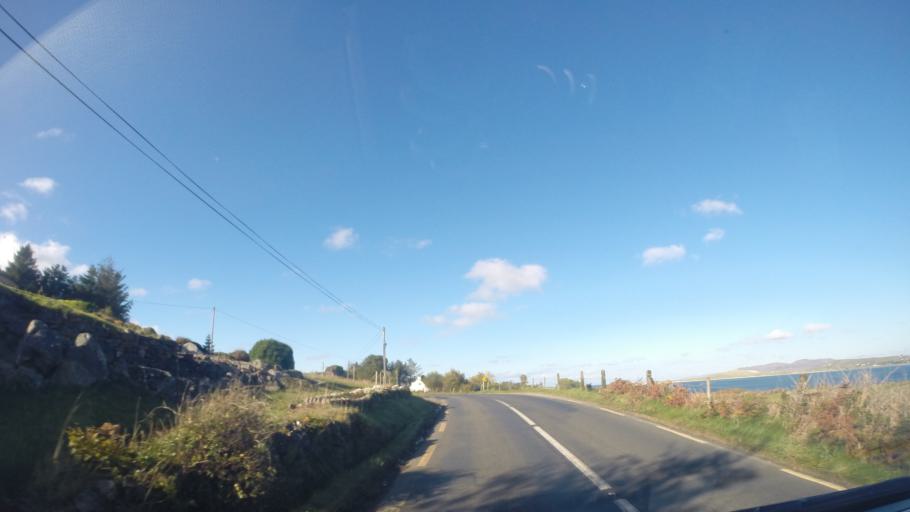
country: IE
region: Ulster
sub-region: County Donegal
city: Dungloe
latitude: 54.8338
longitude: -8.3500
